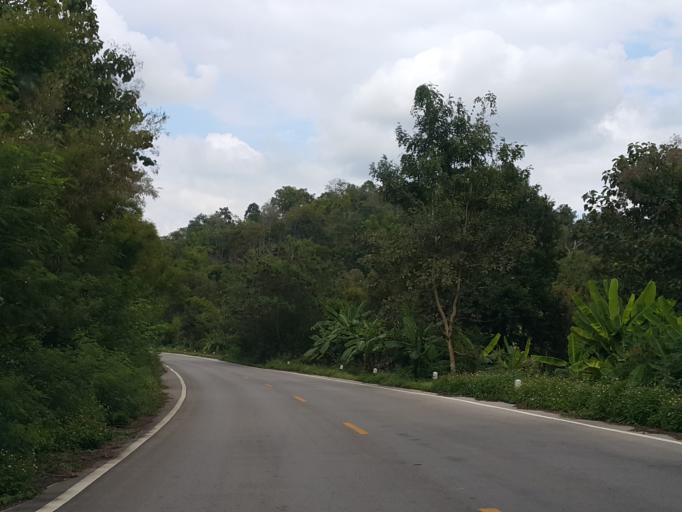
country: TH
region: Lampang
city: Chae Hom
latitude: 18.6268
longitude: 99.4892
